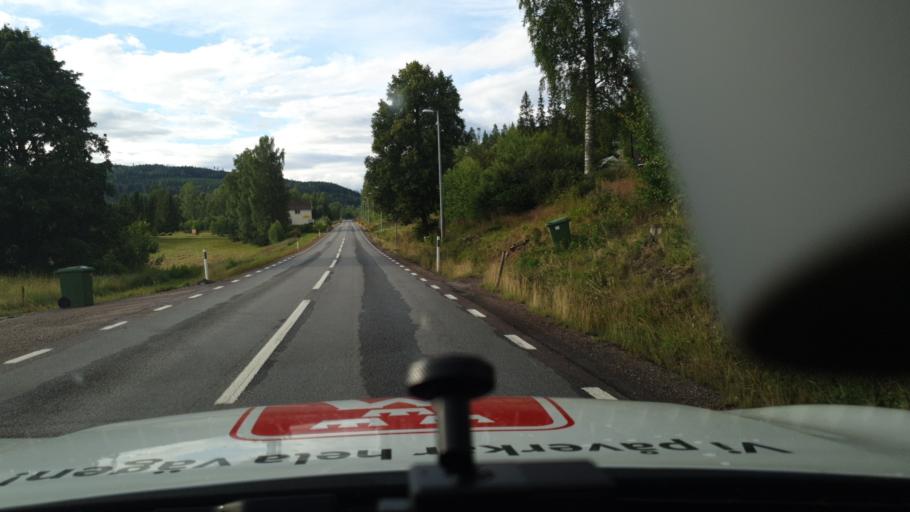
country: SE
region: Vaermland
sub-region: Torsby Kommun
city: Torsby
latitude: 60.2341
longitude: 13.0121
